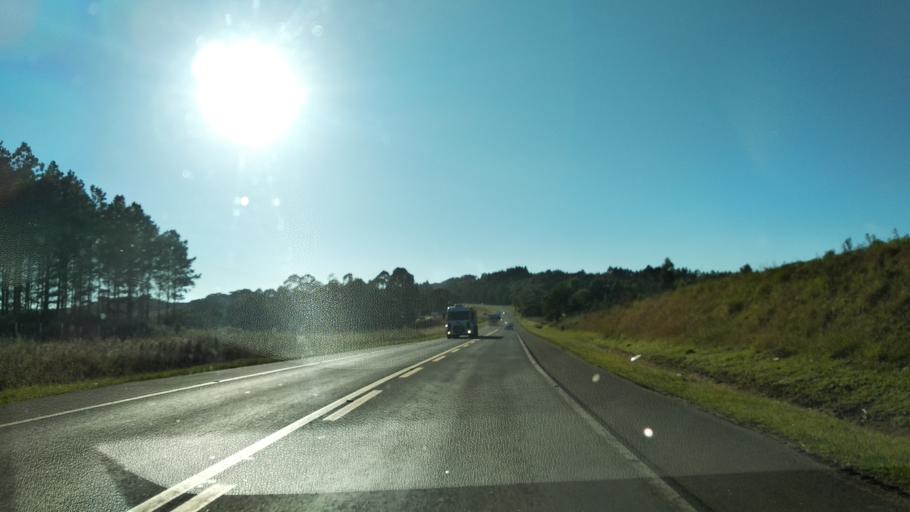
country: BR
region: Santa Catarina
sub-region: Lages
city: Lages
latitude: -27.7955
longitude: -50.3901
